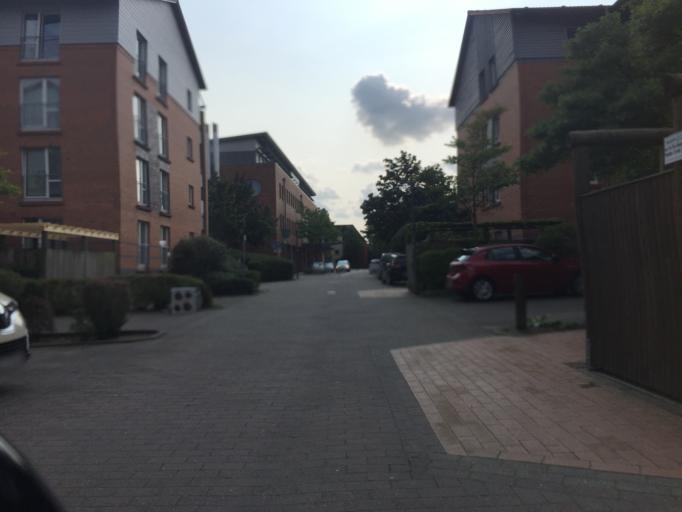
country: DE
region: Schleswig-Holstein
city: Itzehoe
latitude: 53.9325
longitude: 9.5261
